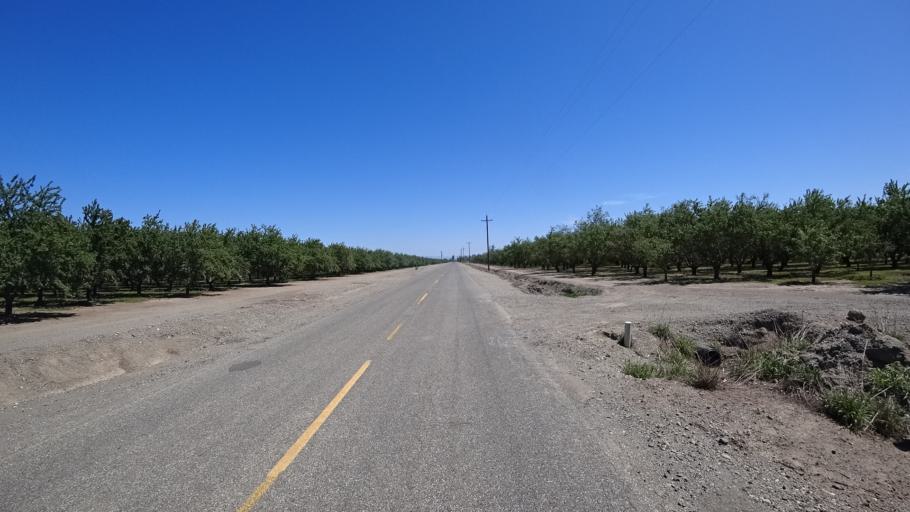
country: US
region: California
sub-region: Glenn County
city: Orland
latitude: 39.7251
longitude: -122.1317
